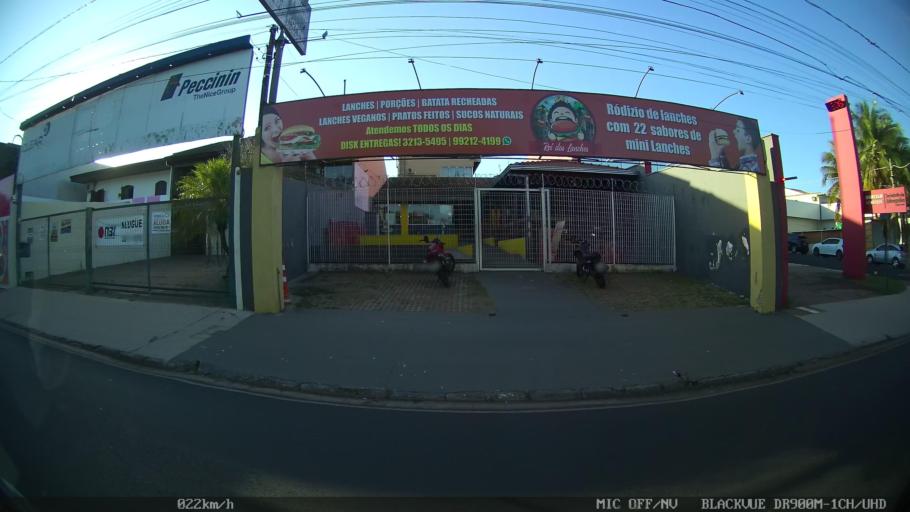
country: BR
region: Sao Paulo
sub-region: Sao Jose Do Rio Preto
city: Sao Jose do Rio Preto
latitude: -20.8064
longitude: -49.3628
